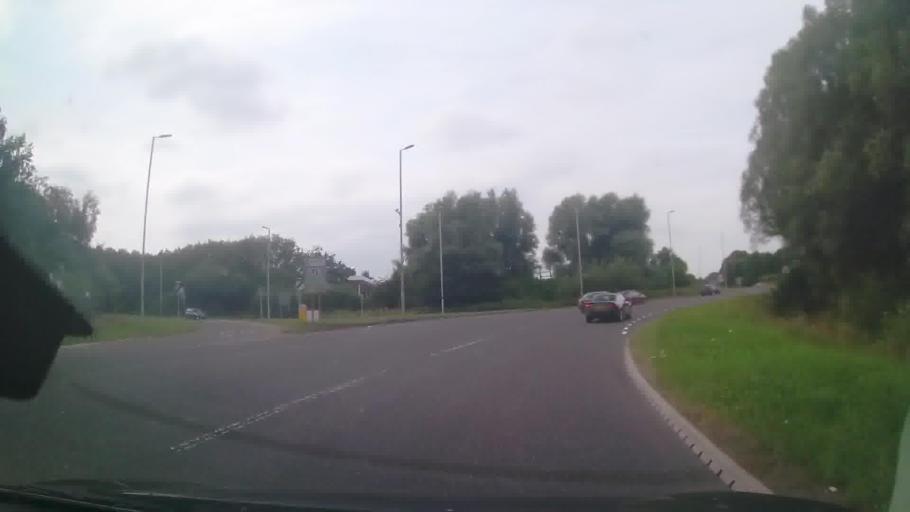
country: GB
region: England
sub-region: Leicestershire
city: Markfield
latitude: 52.6950
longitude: -1.2929
